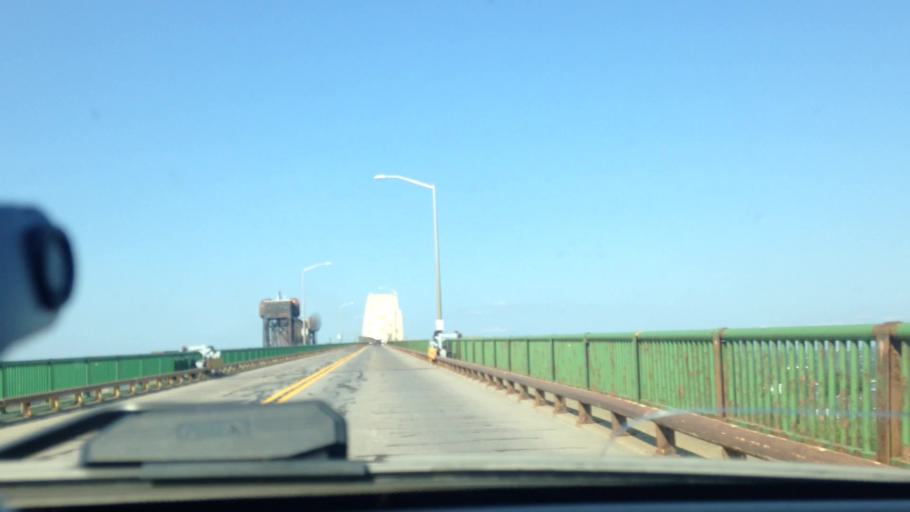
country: US
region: Michigan
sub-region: Chippewa County
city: Sault Ste. Marie
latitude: 46.4984
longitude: -84.3647
